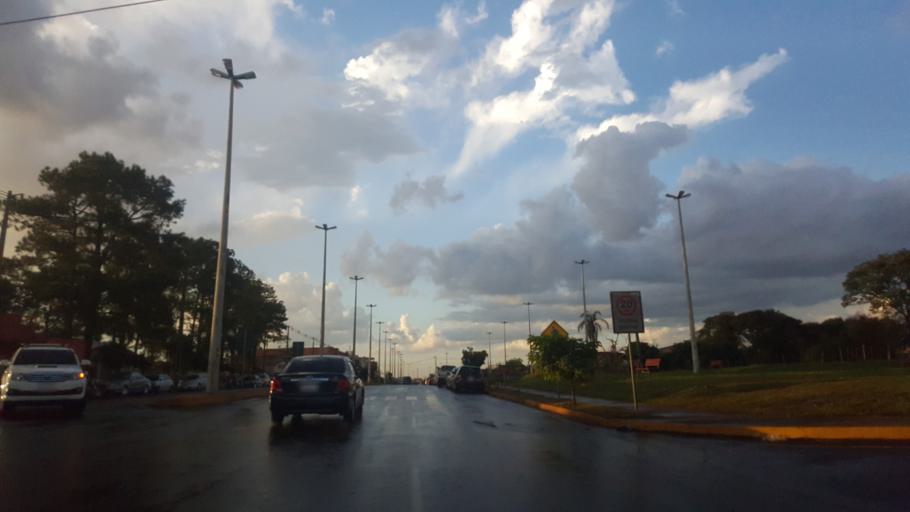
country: PY
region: Itapua
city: Encarnacion
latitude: -27.3578
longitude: -55.8587
